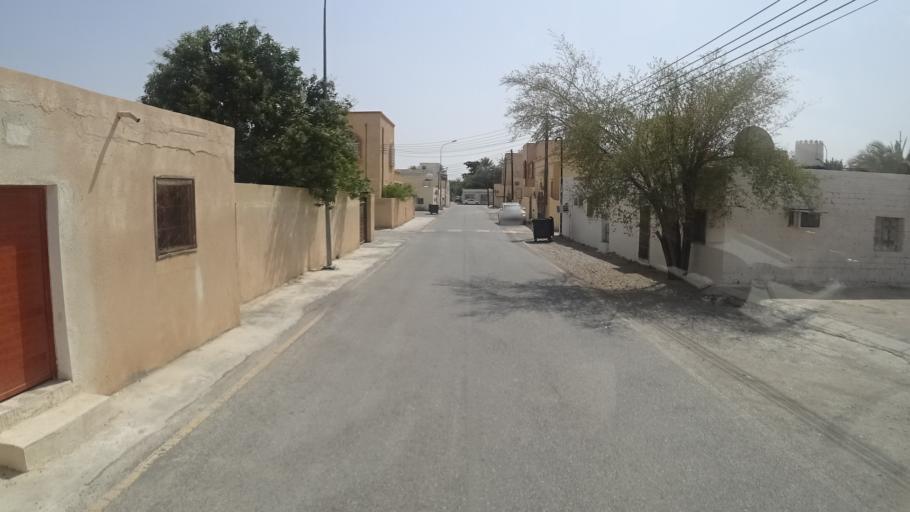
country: OM
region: Muhafazat ad Dakhiliyah
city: Bahla'
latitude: 23.1197
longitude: 57.2930
